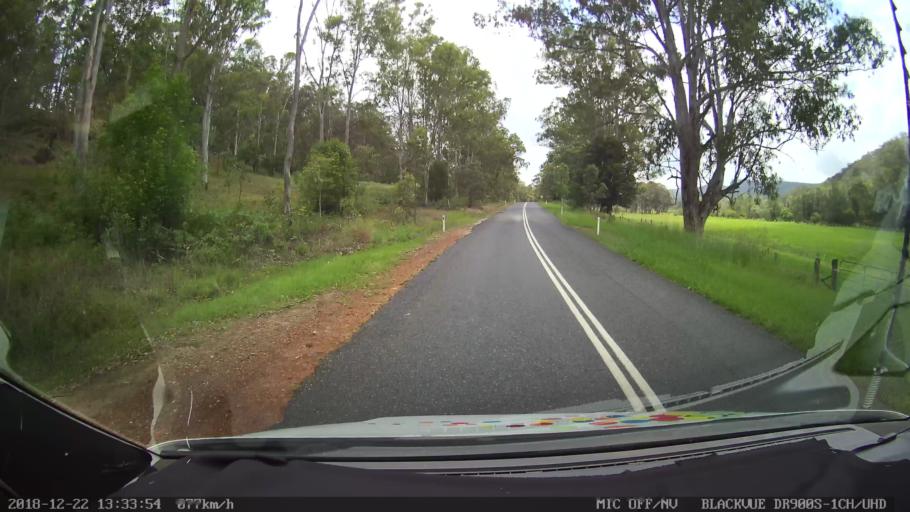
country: AU
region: New South Wales
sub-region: Clarence Valley
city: Coutts Crossing
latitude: -29.8663
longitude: 152.8233
